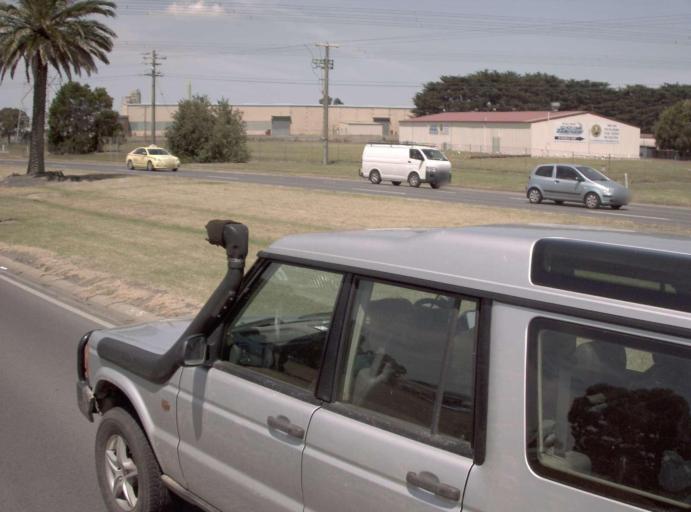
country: AU
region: Victoria
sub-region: Latrobe
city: Morwell
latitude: -38.2330
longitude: 146.4389
